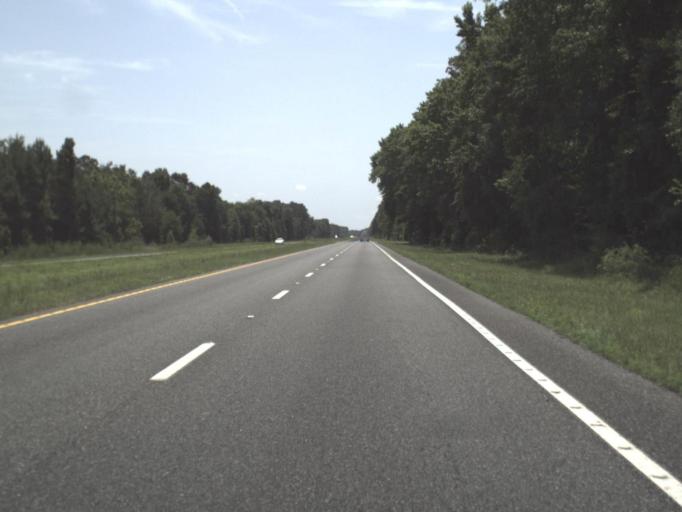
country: US
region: Florida
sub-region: Taylor County
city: Steinhatchee
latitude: 29.9007
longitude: -83.4230
